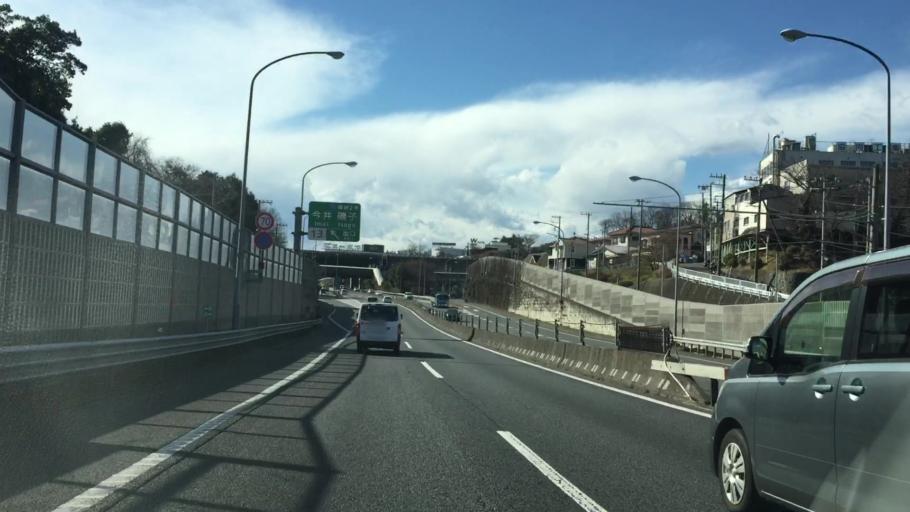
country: JP
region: Kanagawa
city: Yokohama
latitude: 35.4448
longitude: 139.5636
